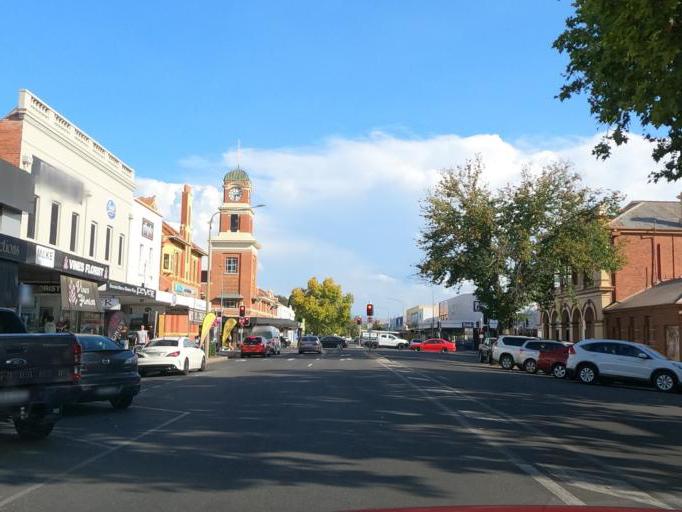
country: AU
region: New South Wales
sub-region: Albury Municipality
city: Albury
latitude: -36.0804
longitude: 146.9183
